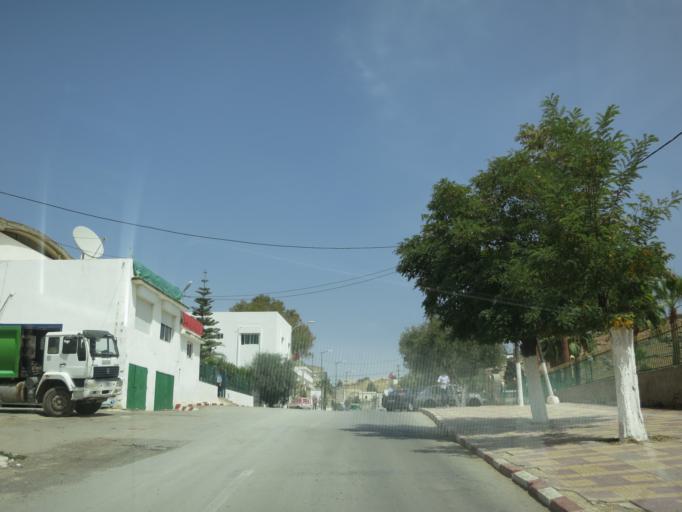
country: MA
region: Meknes-Tafilalet
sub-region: Meknes
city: Meknes
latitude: 34.0576
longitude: -5.5183
